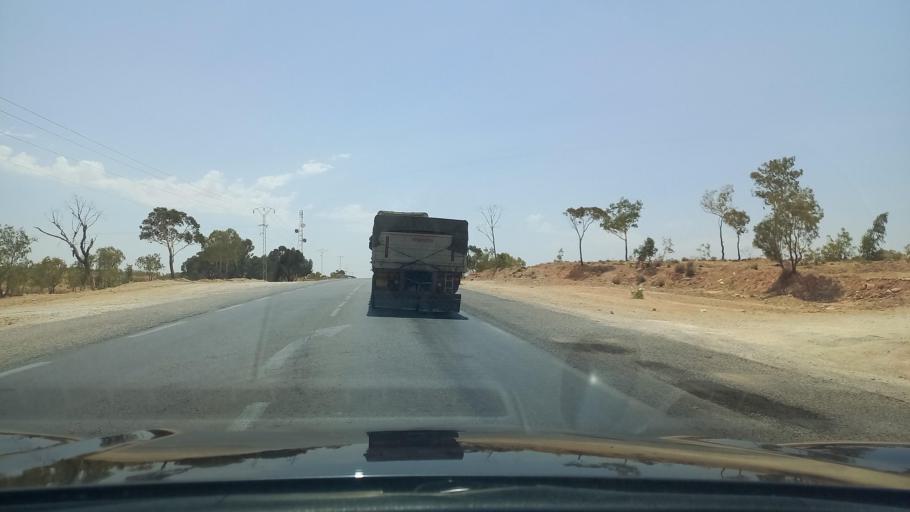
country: TN
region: Madanin
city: Medenine
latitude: 33.5726
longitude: 10.3171
